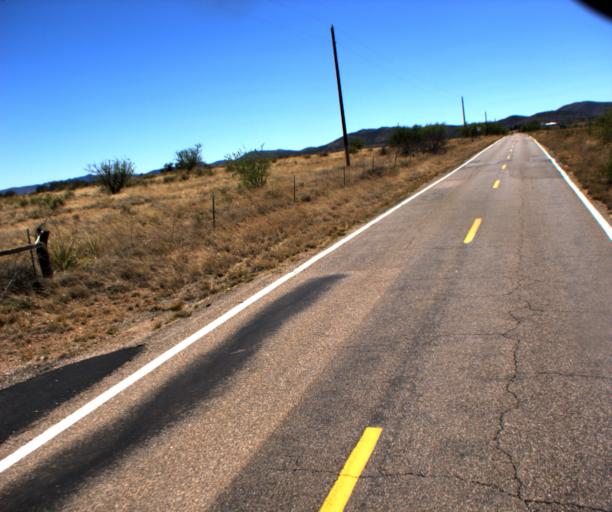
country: US
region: Arizona
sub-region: Cochise County
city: Huachuca City
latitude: 31.5936
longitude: -110.5596
